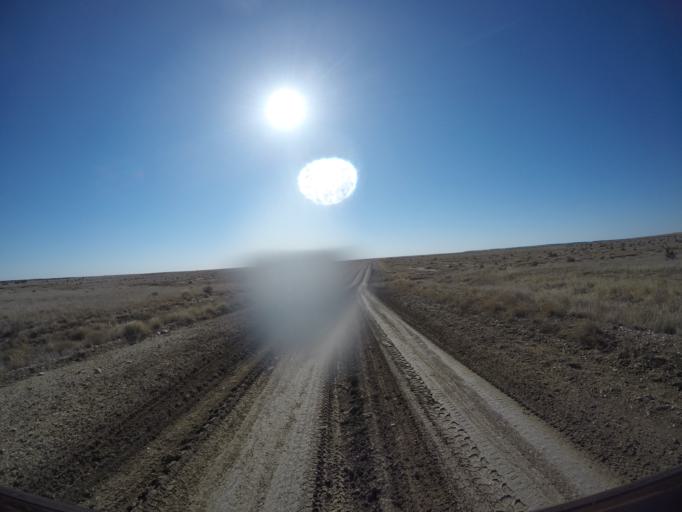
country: US
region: Colorado
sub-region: Otero County
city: La Junta
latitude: 37.7143
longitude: -103.6205
